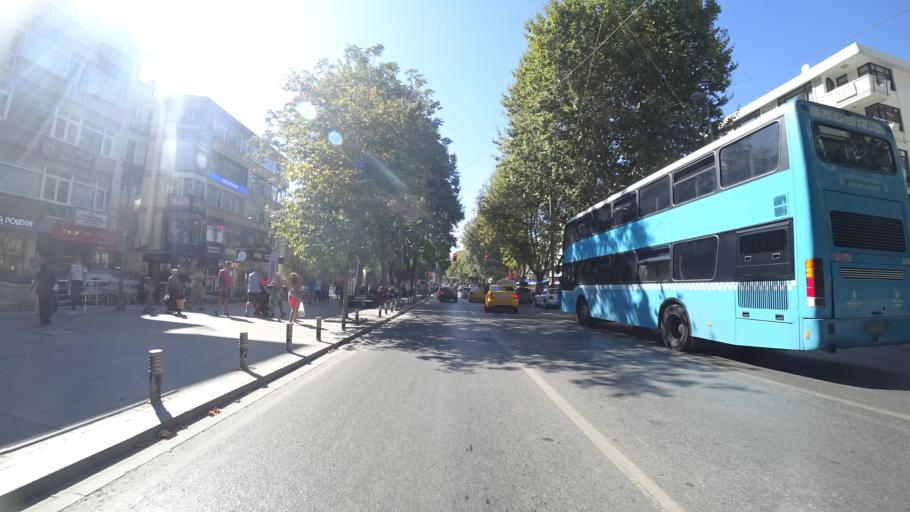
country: TR
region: Istanbul
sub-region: Atasehir
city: Atasehir
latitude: 40.9631
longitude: 29.0754
